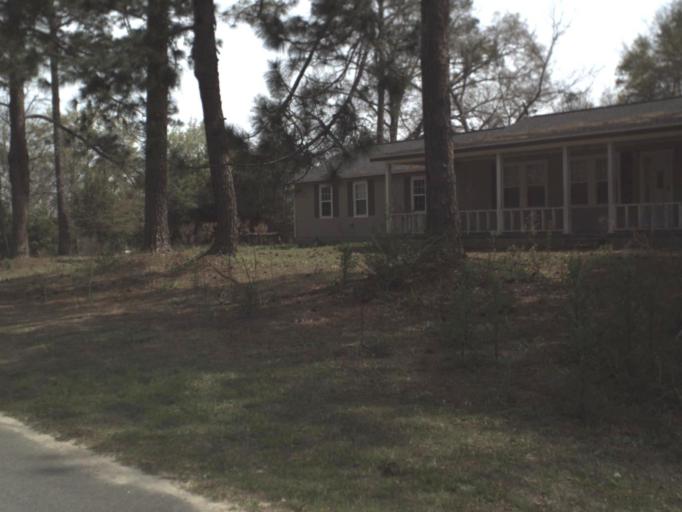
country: US
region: Florida
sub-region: Jackson County
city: Graceville
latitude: 30.9648
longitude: -85.5267
